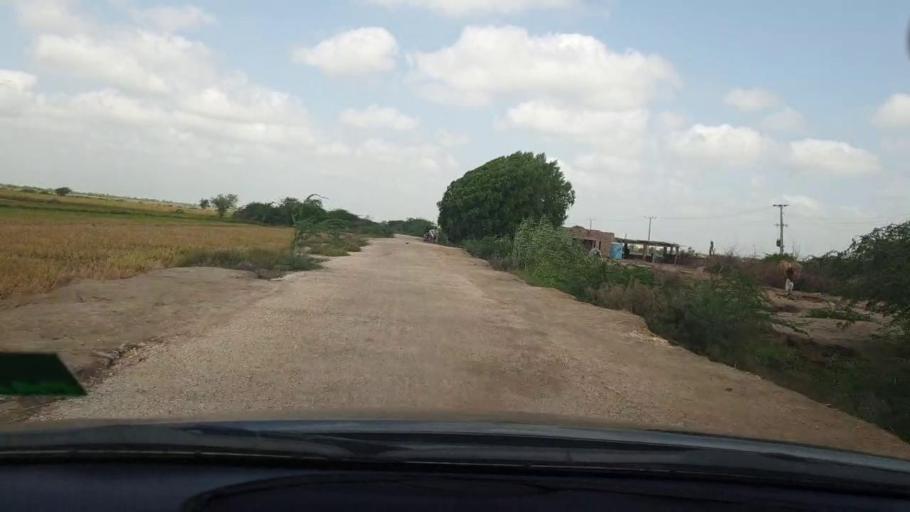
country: PK
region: Sindh
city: Tando Bago
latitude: 24.8552
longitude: 69.0338
